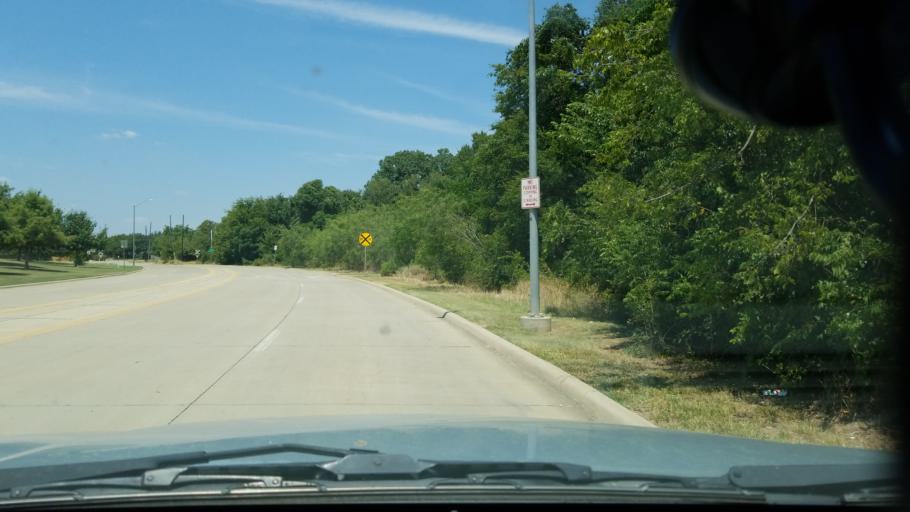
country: US
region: Texas
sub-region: Dallas County
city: Grand Prairie
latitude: 32.7599
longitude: -96.9539
